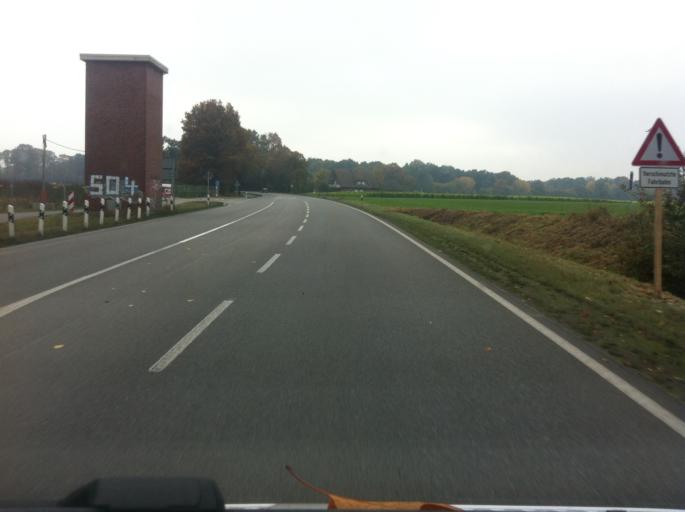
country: DE
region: North Rhine-Westphalia
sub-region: Regierungsbezirk Munster
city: Vreden
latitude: 52.0200
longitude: 6.8232
